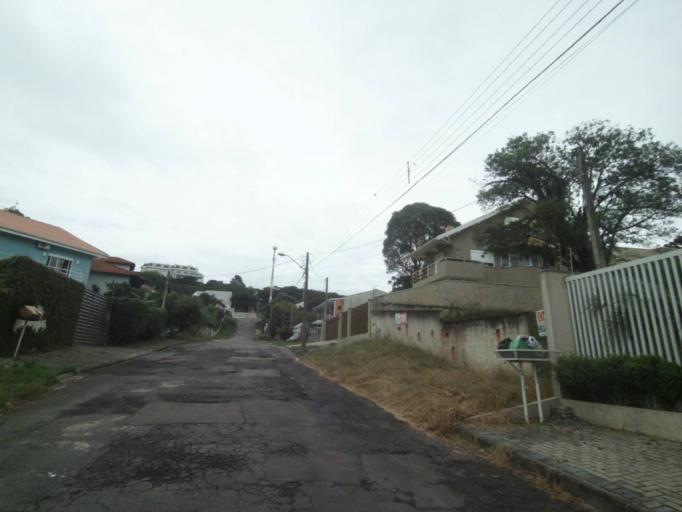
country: BR
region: Parana
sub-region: Curitiba
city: Curitiba
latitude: -25.4485
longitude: -49.3171
